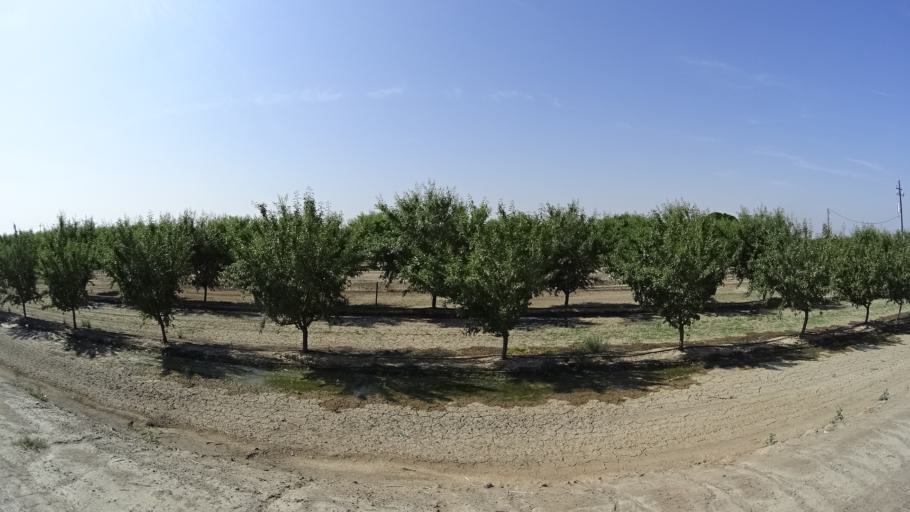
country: US
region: California
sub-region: Kings County
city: Lemoore
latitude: 36.3134
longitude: -119.8107
